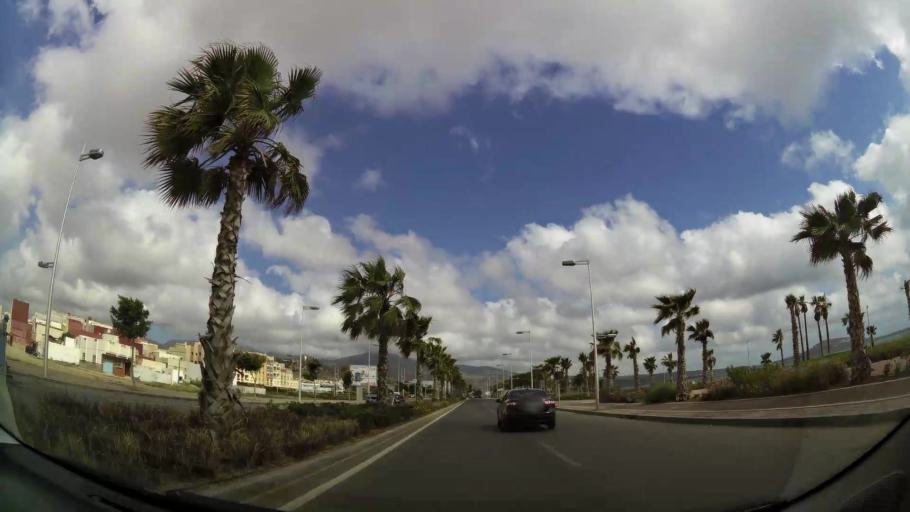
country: MA
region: Oriental
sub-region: Nador
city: Nador
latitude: 35.1731
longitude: -2.9164
